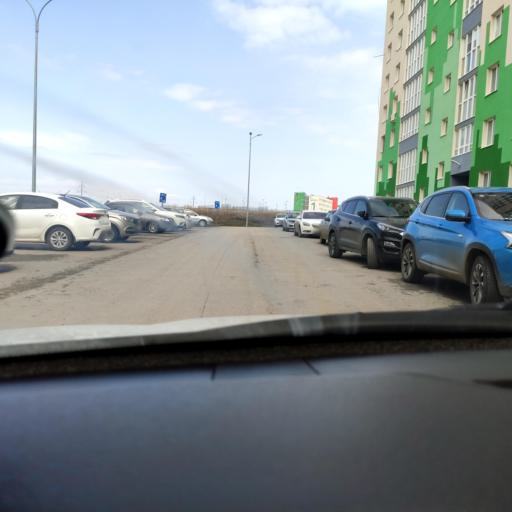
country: RU
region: Samara
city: Petra-Dubrava
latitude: 53.3020
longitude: 50.3256
